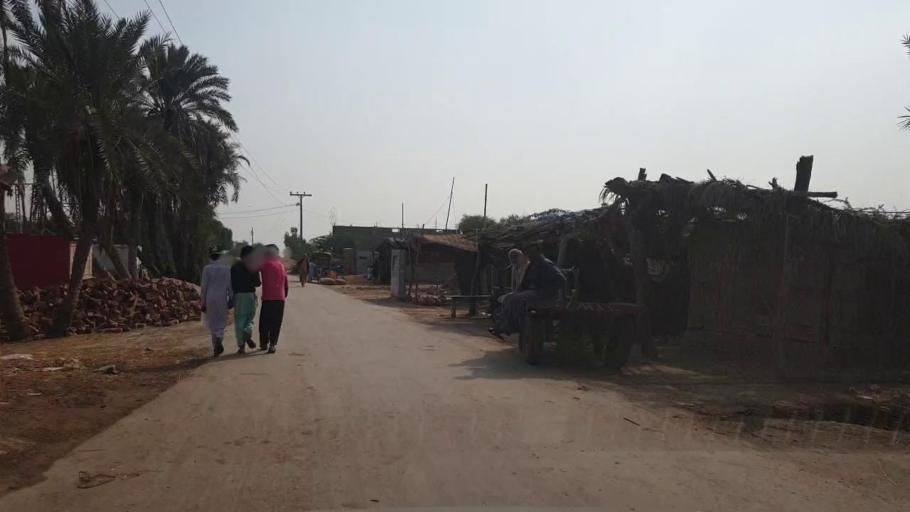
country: PK
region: Sindh
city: Tando Muhammad Khan
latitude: 25.1109
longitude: 68.3629
